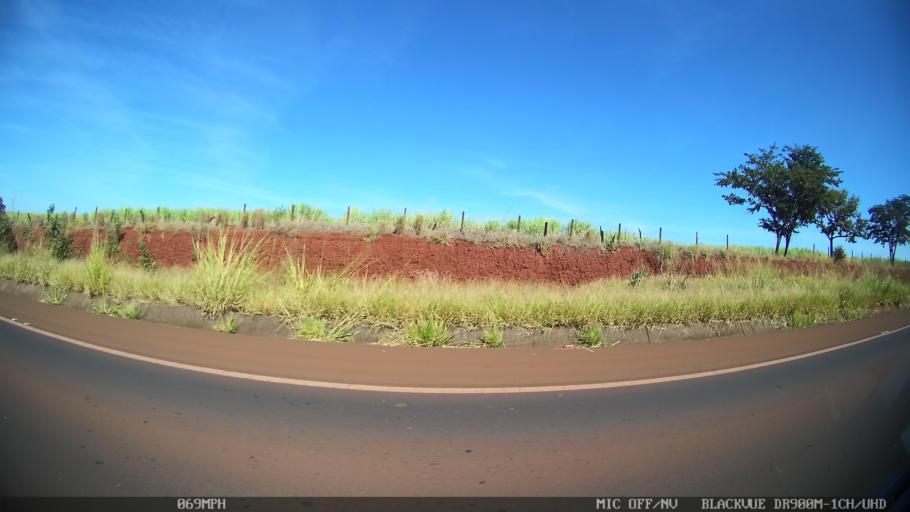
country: BR
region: Sao Paulo
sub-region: Sao Joaquim Da Barra
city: Sao Joaquim da Barra
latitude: -20.5465
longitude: -47.7736
